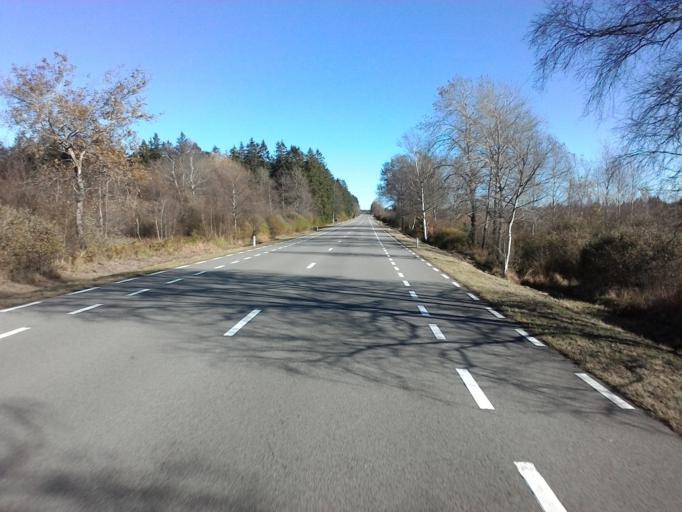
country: BE
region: Wallonia
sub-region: Province de Liege
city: Malmedy
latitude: 50.4906
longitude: 6.0630
